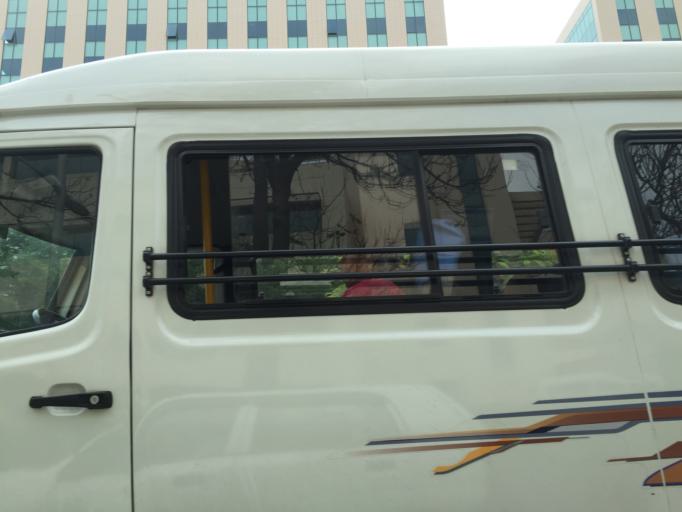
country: IN
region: Karnataka
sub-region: Bangalore Urban
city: Yelahanka
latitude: 13.0438
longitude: 77.6191
